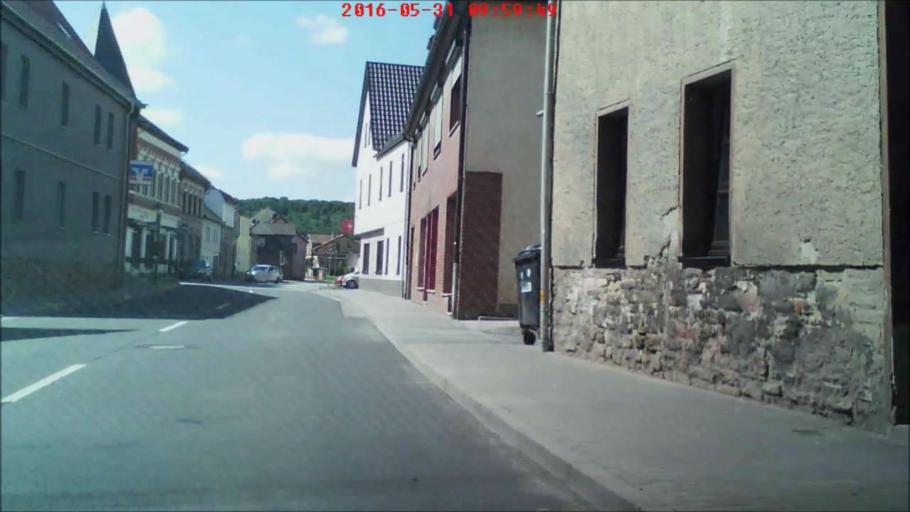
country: DE
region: Thuringia
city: Heldrungen
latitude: 51.3014
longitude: 11.2169
